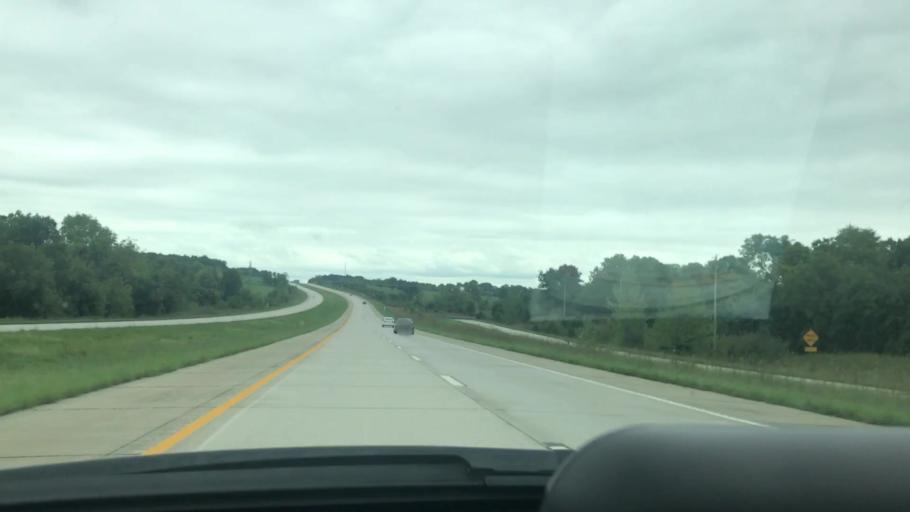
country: US
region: Missouri
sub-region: Dallas County
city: Buffalo
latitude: 37.5266
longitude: -93.1376
